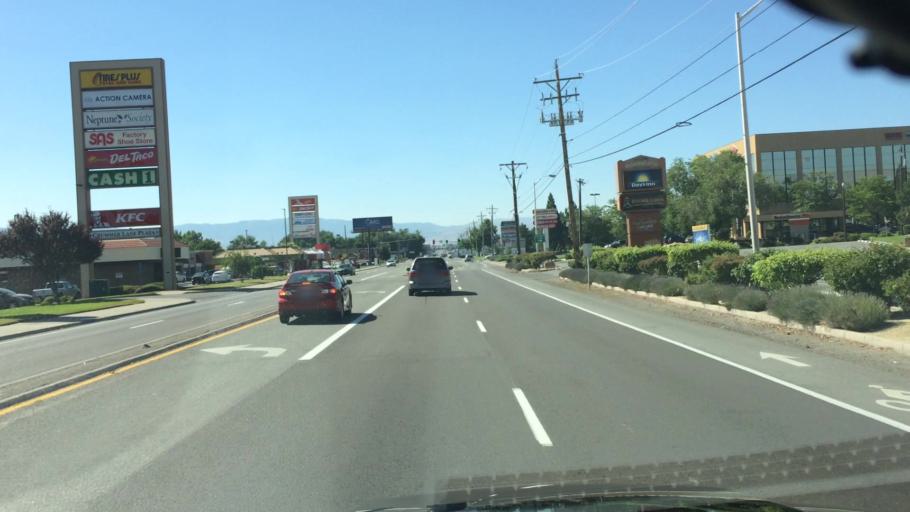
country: US
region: Nevada
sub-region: Washoe County
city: Reno
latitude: 39.4732
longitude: -119.7874
